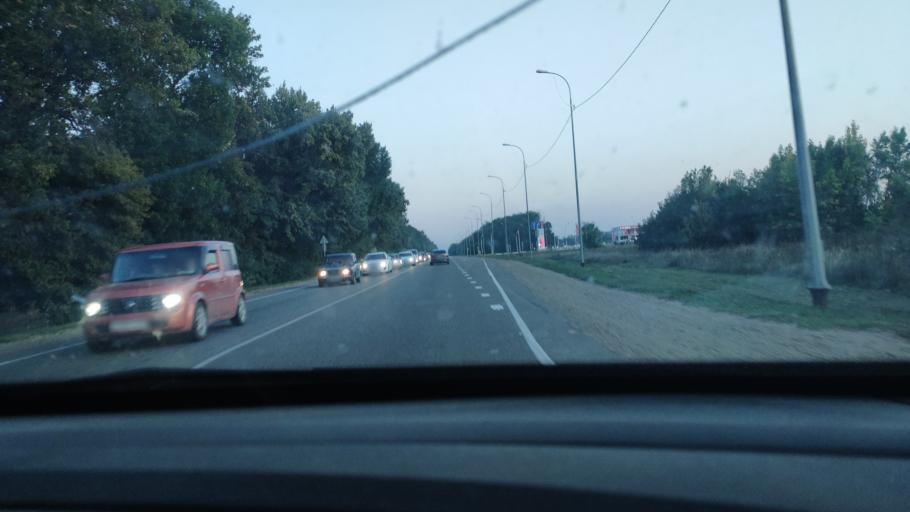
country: RU
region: Krasnodarskiy
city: Medvedovskaya
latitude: 45.4474
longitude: 38.9931
